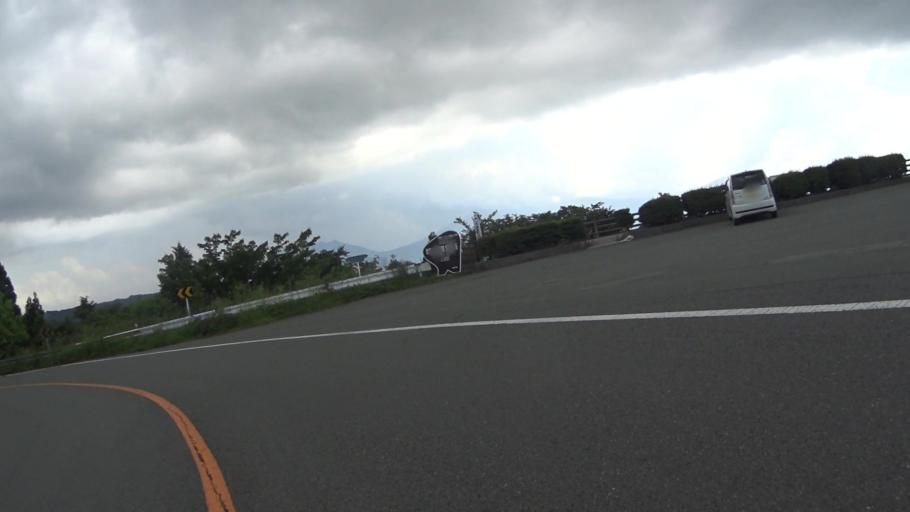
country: JP
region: Kumamoto
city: Aso
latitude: 32.9762
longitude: 131.1402
